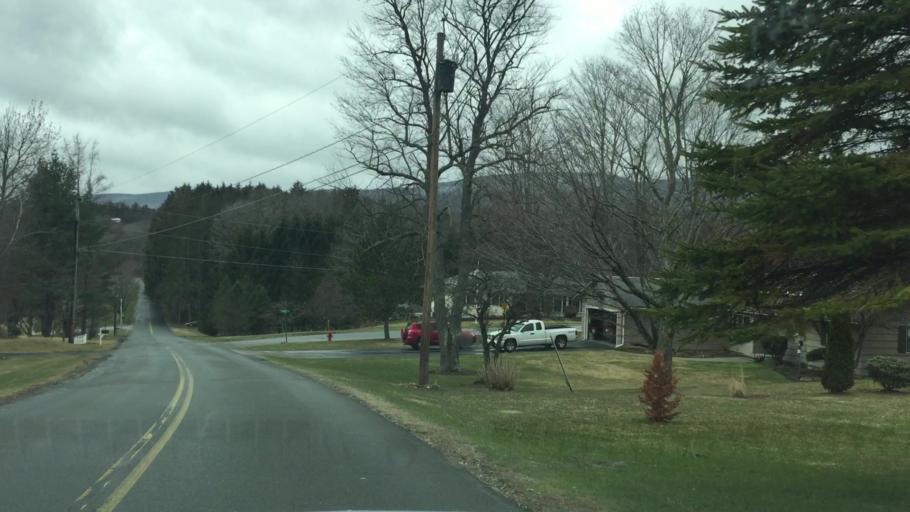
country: US
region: Massachusetts
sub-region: Berkshire County
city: Lanesborough
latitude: 42.5101
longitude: -73.2598
